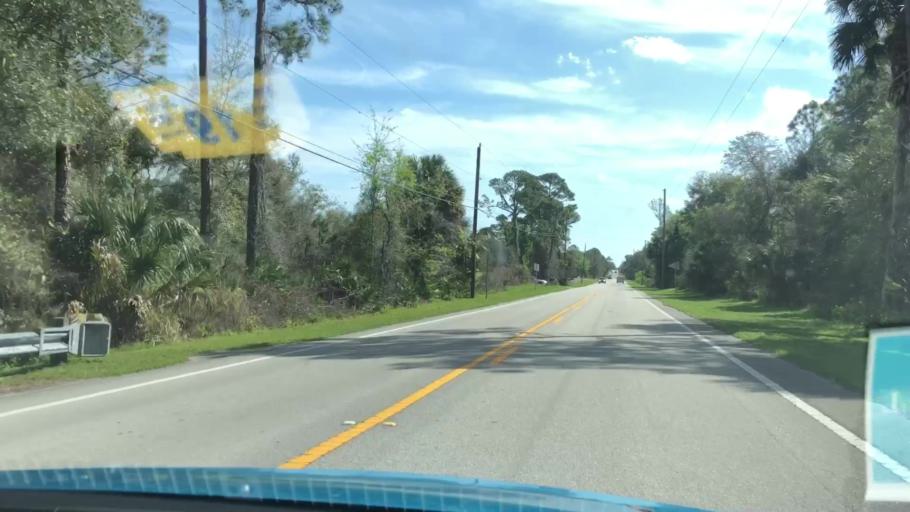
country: US
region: Florida
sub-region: Volusia County
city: Deltona
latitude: 28.8624
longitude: -81.2067
